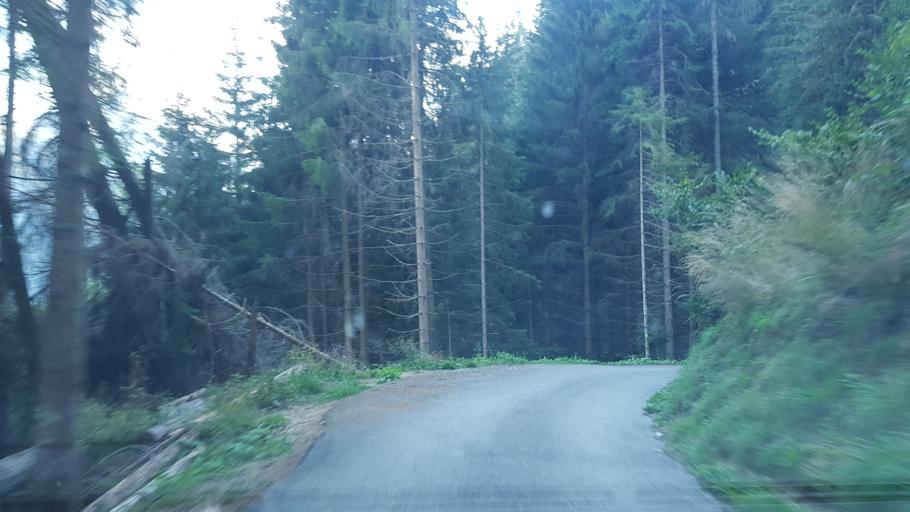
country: IT
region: Veneto
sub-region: Provincia di Belluno
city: San Pietro di Cadore
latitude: 46.5882
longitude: 12.5918
